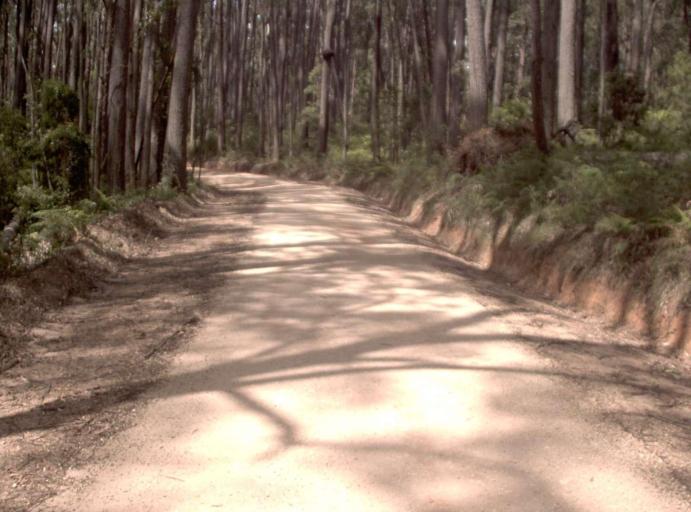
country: AU
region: Victoria
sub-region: East Gippsland
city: Lakes Entrance
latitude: -37.5926
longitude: 148.7206
